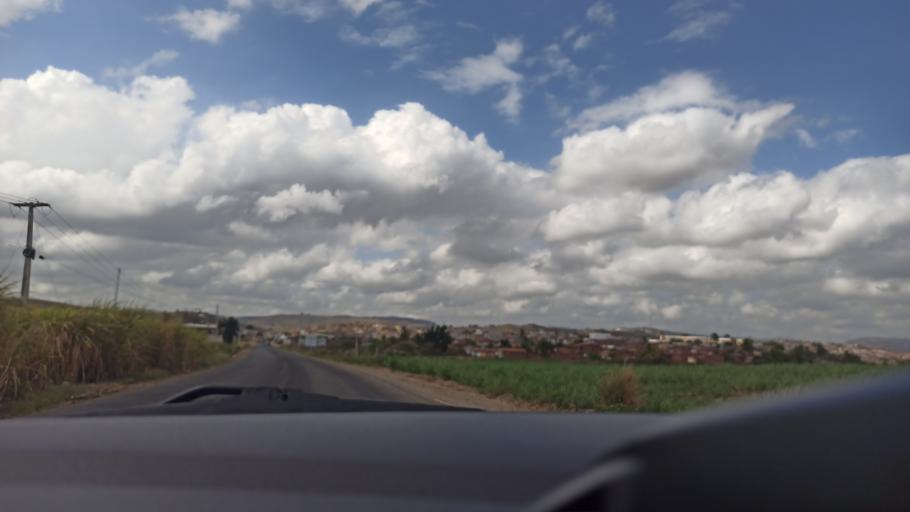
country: BR
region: Pernambuco
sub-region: Timbauba
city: Timbauba
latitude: -7.4908
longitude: -35.2966
